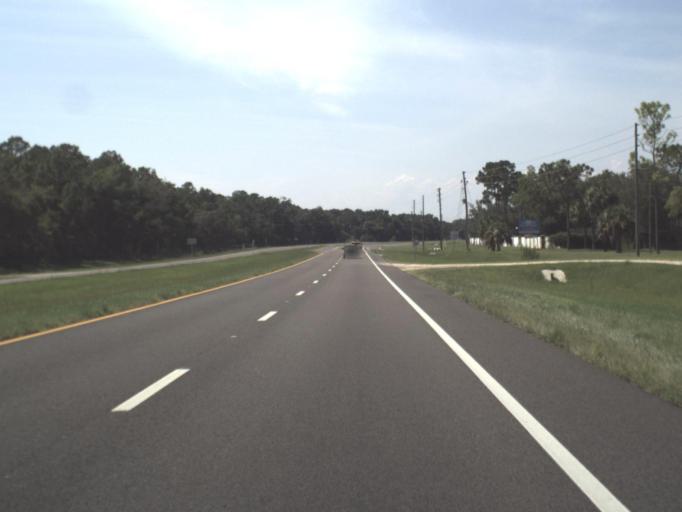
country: US
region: Florida
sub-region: Levy County
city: Inglis
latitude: 29.0171
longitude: -82.6663
